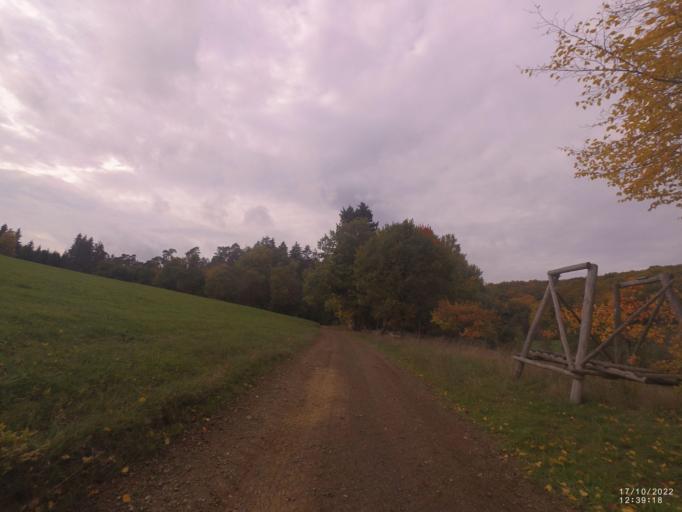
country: DE
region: Rheinland-Pfalz
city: Utzerath
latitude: 50.2116
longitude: 6.9314
